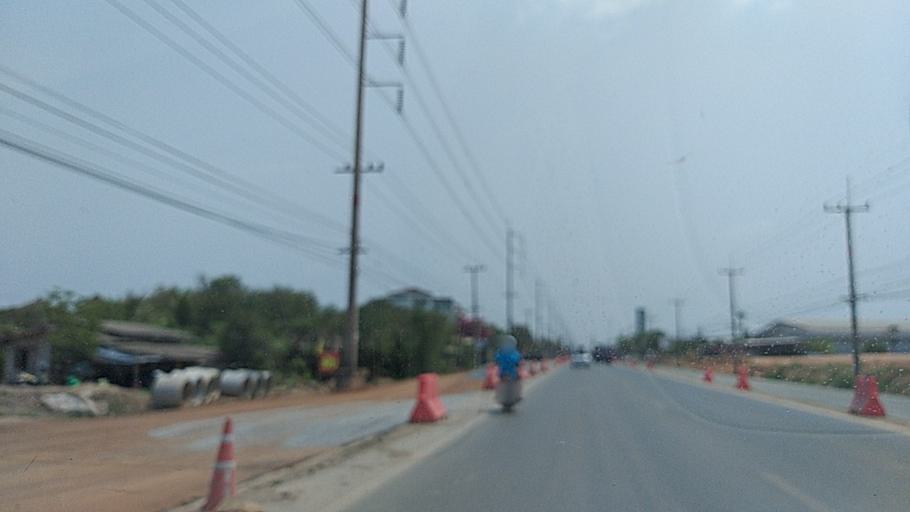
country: TH
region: Chachoengsao
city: Ban Pho
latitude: 13.5985
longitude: 101.1184
